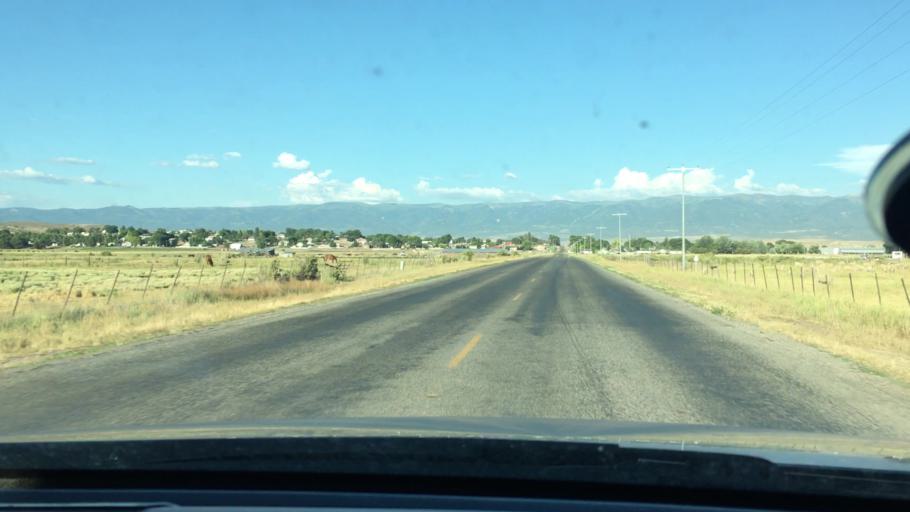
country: US
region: Utah
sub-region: Sanpete County
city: Moroni
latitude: 39.5235
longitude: -111.6052
